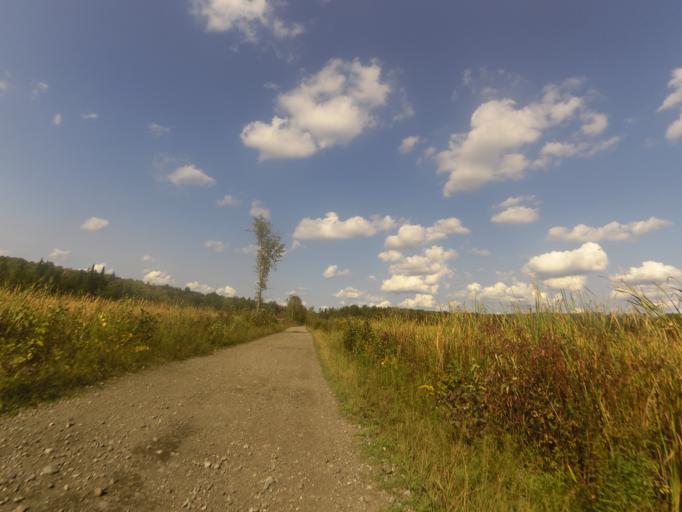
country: CA
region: Ontario
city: Renfrew
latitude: 45.1343
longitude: -76.6866
